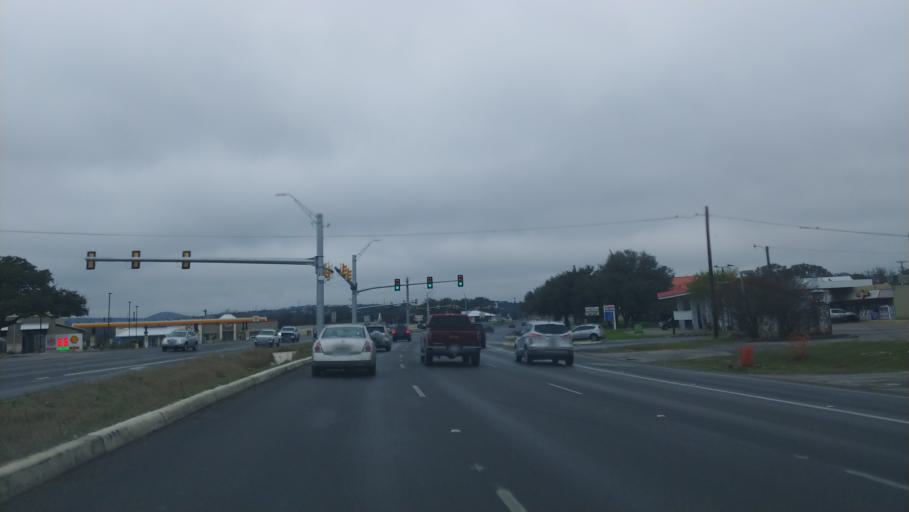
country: US
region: Texas
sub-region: Bexar County
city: Helotes
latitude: 29.5639
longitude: -98.6867
